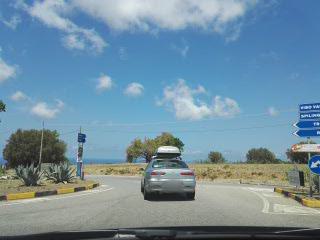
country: IT
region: Calabria
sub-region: Provincia di Vibo-Valentia
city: Ricadi
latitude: 38.6242
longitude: 15.8853
